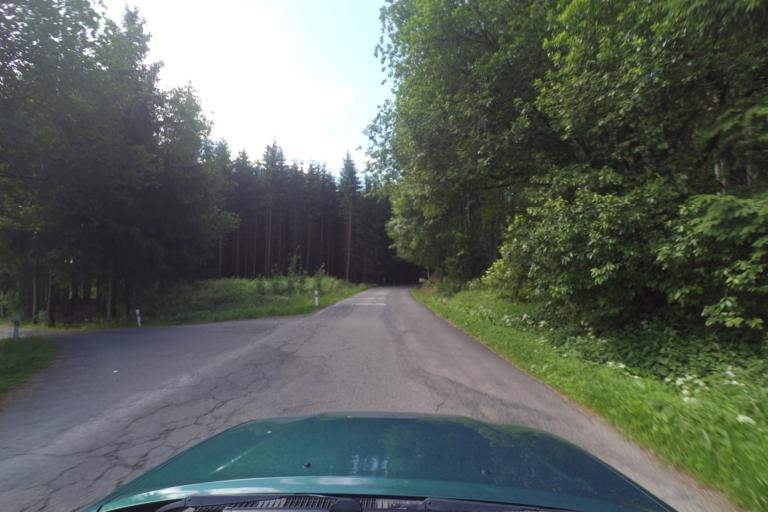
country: CZ
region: Kralovehradecky
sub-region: Okres Nachod
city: Cerveny Kostelec
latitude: 50.4498
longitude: 16.1241
